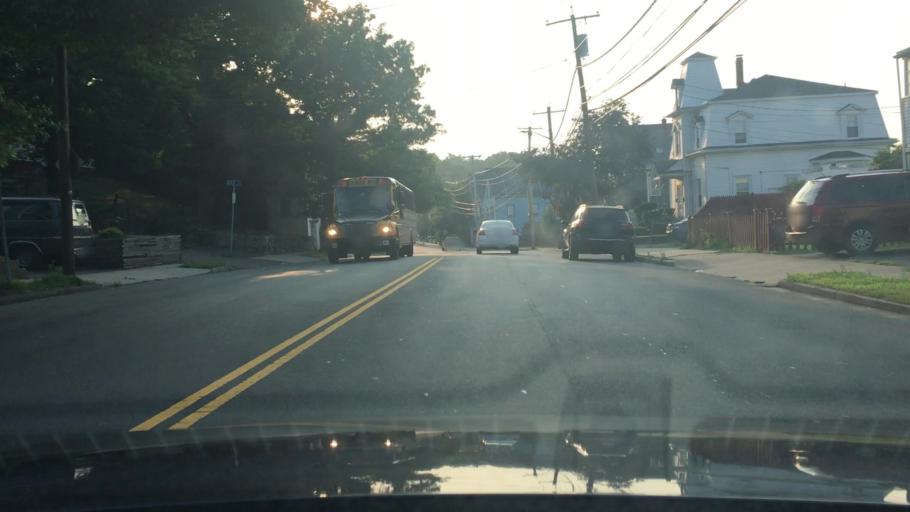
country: US
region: Massachusetts
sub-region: Essex County
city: Lynn
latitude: 42.4695
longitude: -70.9744
